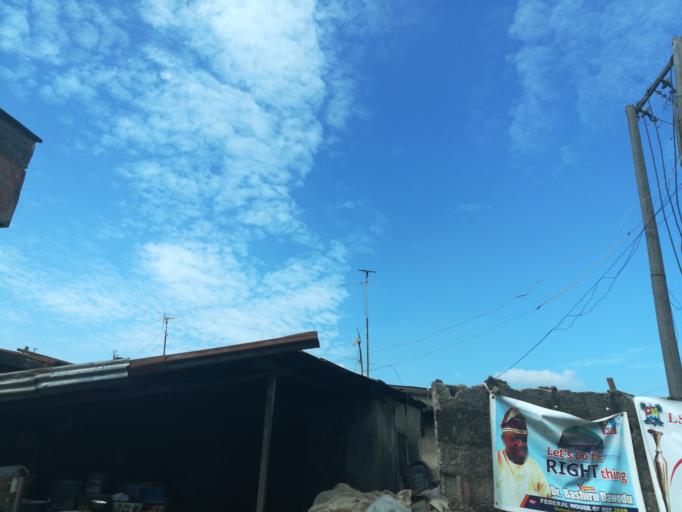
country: NG
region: Lagos
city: Oshodi
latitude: 6.5535
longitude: 3.3336
